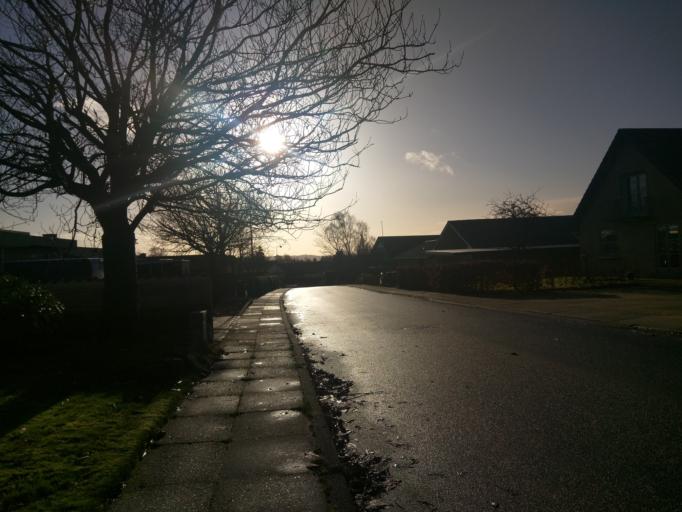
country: DK
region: Central Jutland
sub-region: Silkeborg Kommune
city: Silkeborg
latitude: 56.1856
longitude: 9.5243
